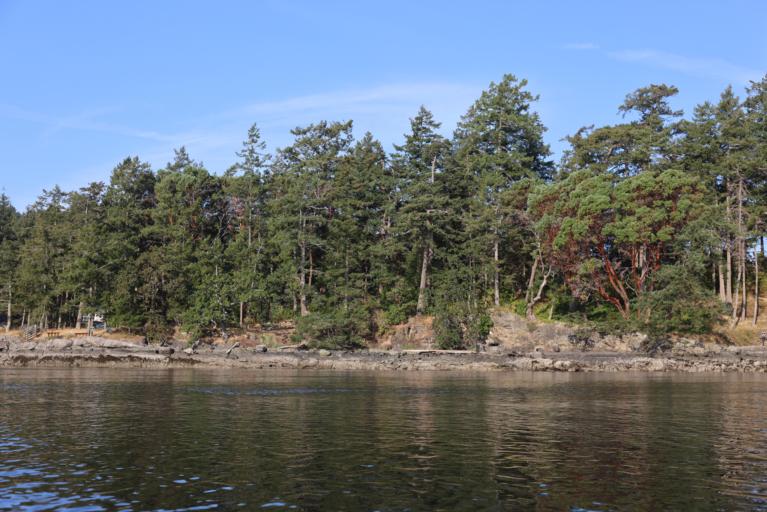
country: CA
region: British Columbia
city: North Saanich
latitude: 48.6811
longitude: -123.3971
